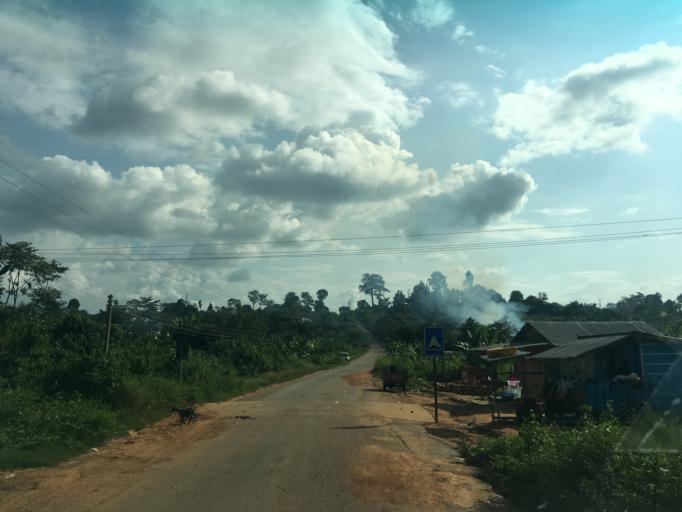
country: GH
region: Western
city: Bibiani
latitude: 6.7959
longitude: -2.5281
